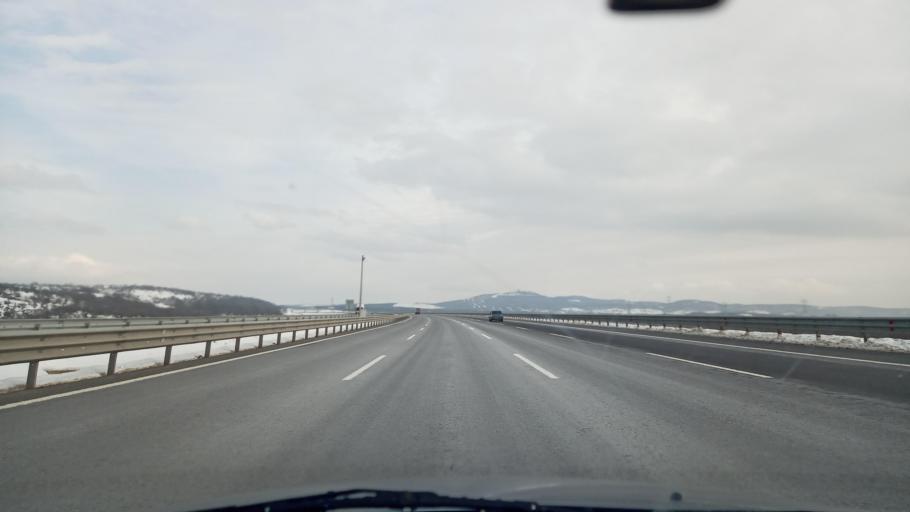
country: TR
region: Kocaeli
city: Mollafeneri
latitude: 40.8883
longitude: 29.5775
